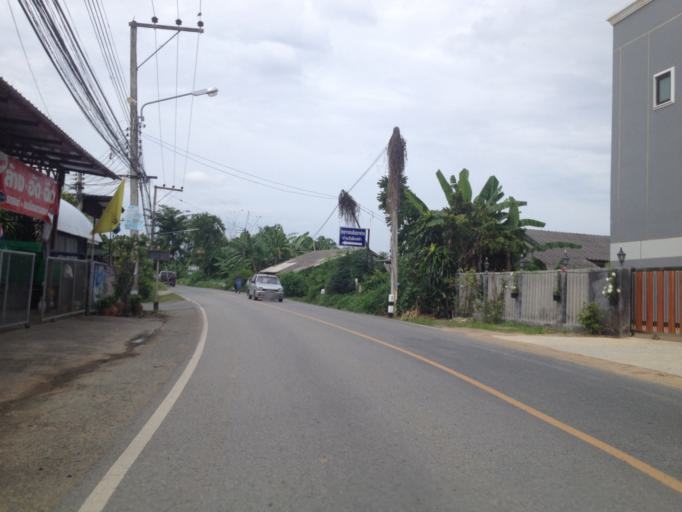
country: TH
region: Chiang Mai
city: Saraphi
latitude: 18.7062
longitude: 98.9833
